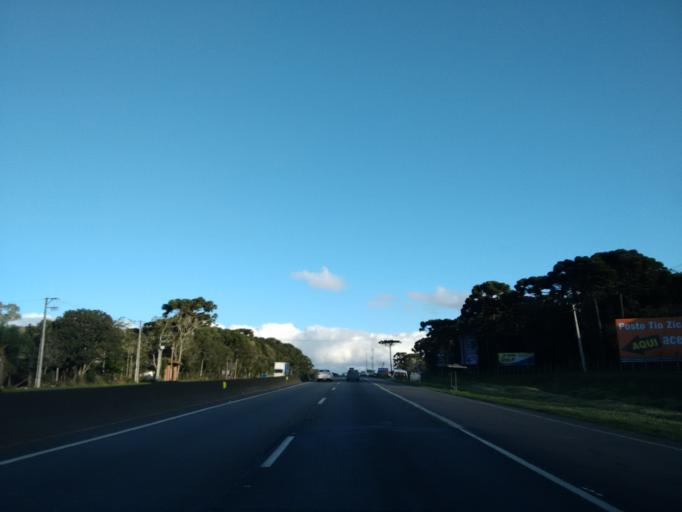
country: BR
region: Parana
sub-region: Sao Jose Dos Pinhais
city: Sao Jose dos Pinhais
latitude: -25.6455
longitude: -49.1589
